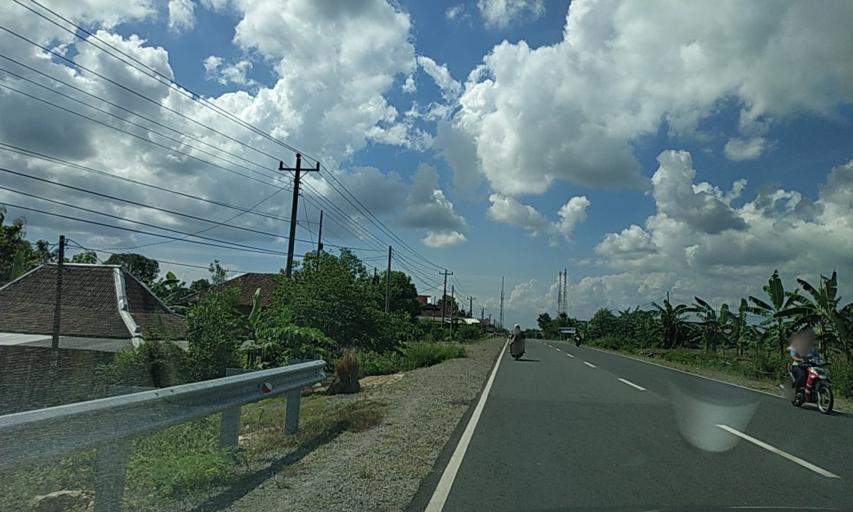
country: ID
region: East Java
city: Krajan
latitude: -8.0235
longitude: 110.8947
